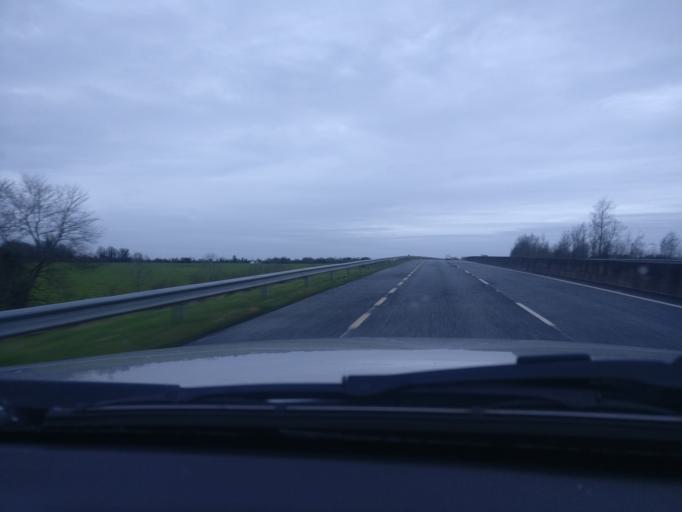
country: IE
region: Leinster
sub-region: An Mhi
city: Navan
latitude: 53.6481
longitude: -6.7173
